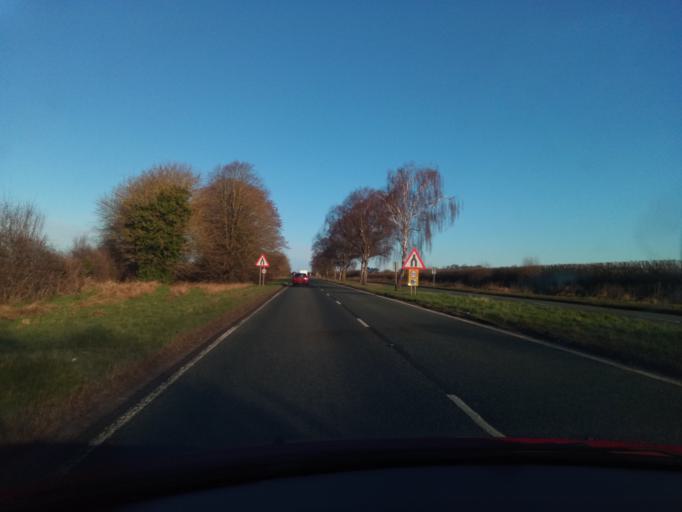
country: GB
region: England
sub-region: Nottinghamshire
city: Farnsfield
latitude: 53.0697
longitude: -1.0703
